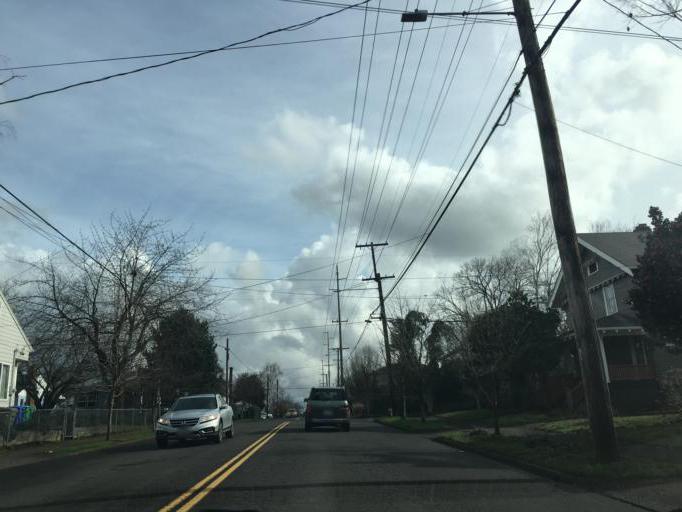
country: US
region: Oregon
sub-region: Clackamas County
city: Milwaukie
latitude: 45.4903
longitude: -122.6175
